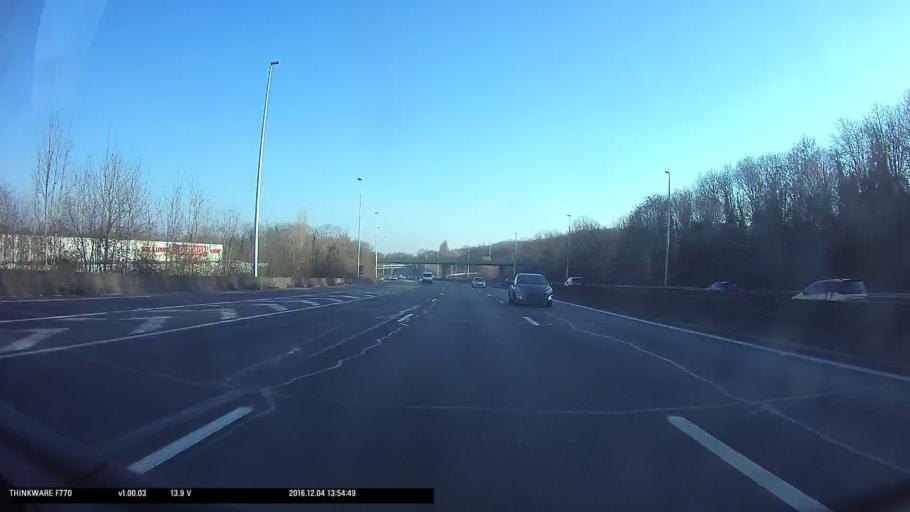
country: FR
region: Ile-de-France
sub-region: Departement du Val-d'Oise
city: Franconville
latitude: 48.9771
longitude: 2.2345
